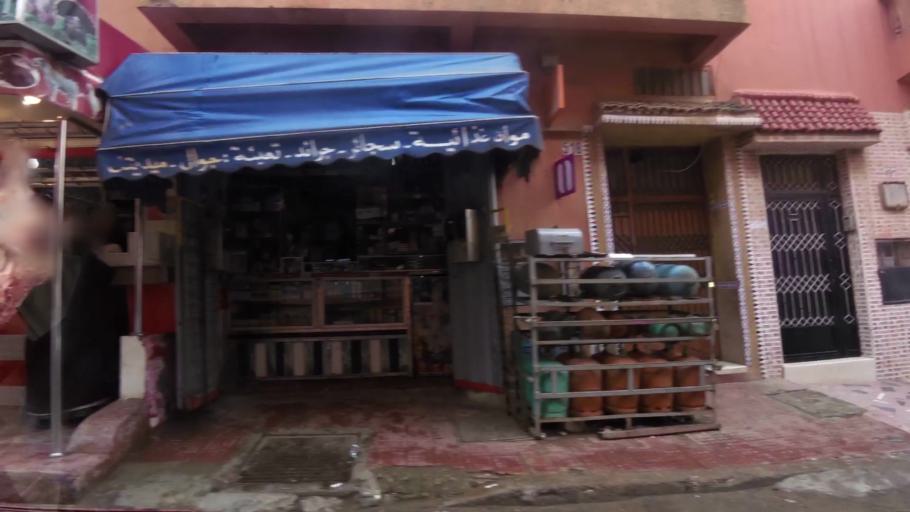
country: MA
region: Grand Casablanca
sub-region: Nouaceur
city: Bouskoura
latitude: 33.5068
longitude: -7.6532
